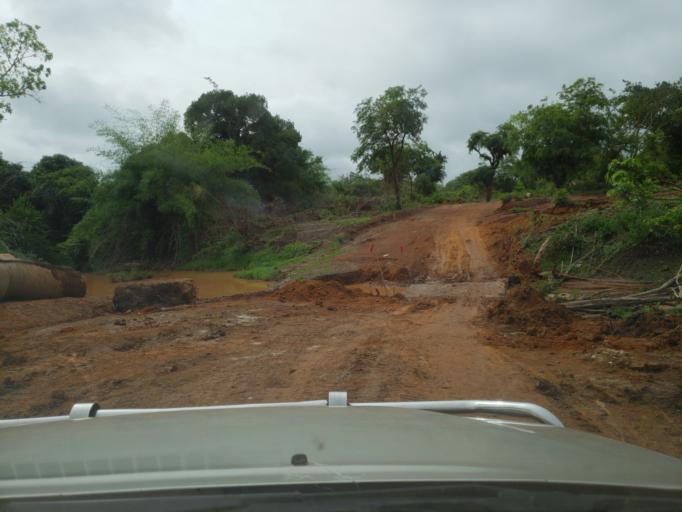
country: ML
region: Koulikoro
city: Kangaba
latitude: 12.0248
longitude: -8.7156
